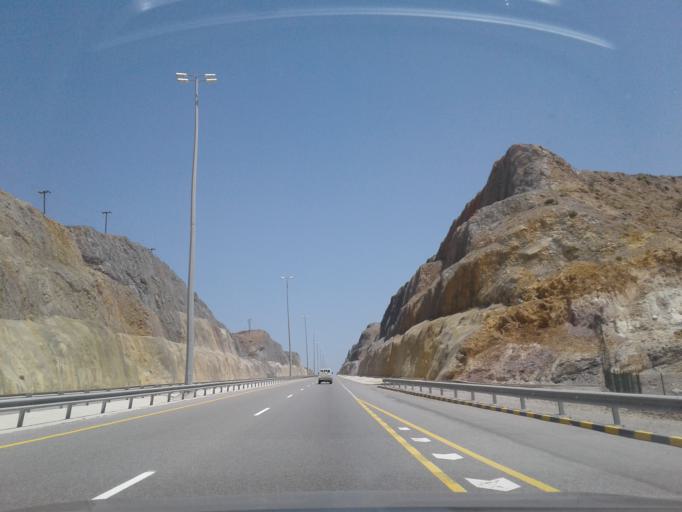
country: OM
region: Muhafazat Masqat
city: Muscat
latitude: 23.2114
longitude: 58.8024
